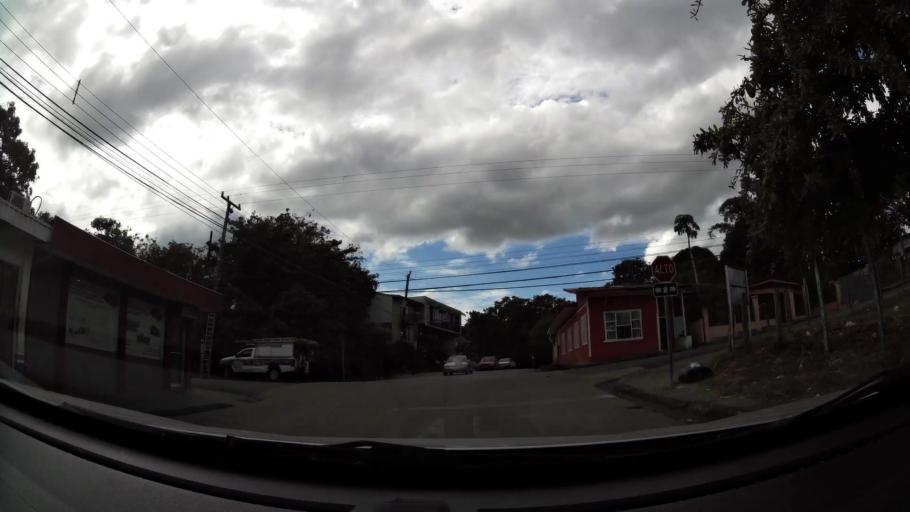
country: CR
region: Guanacaste
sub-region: Canton de Nicoya
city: Nicoya
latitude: 10.1412
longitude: -85.4536
